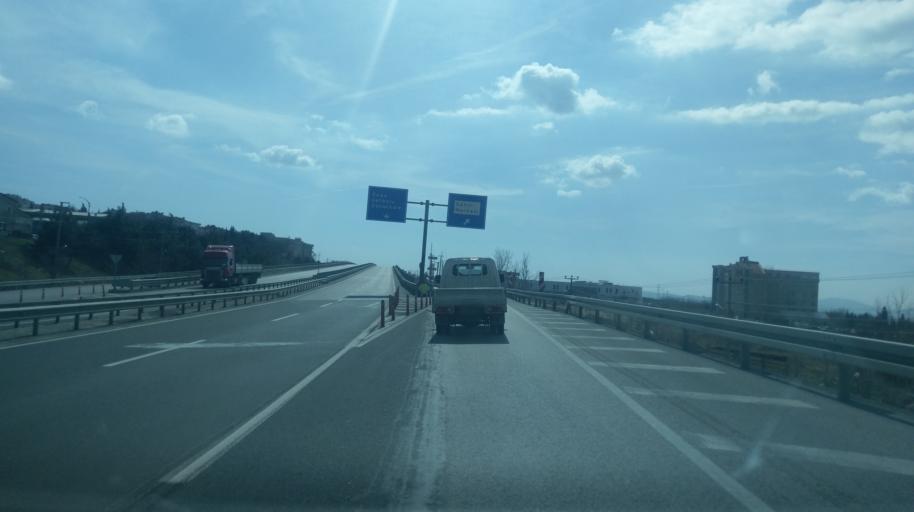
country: TR
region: Edirne
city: Kesan
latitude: 40.8620
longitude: 26.6217
